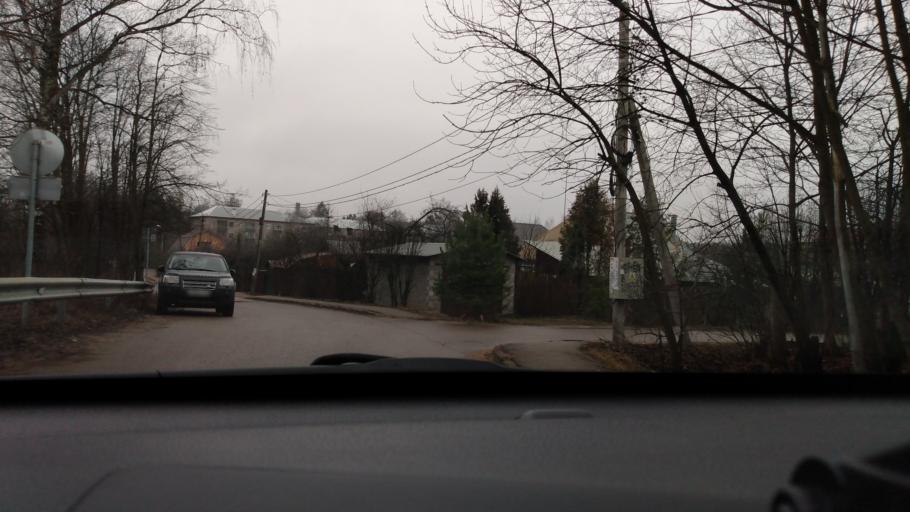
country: RU
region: Moskovskaya
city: Lesnoy Gorodok
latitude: 55.6605
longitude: 37.1796
